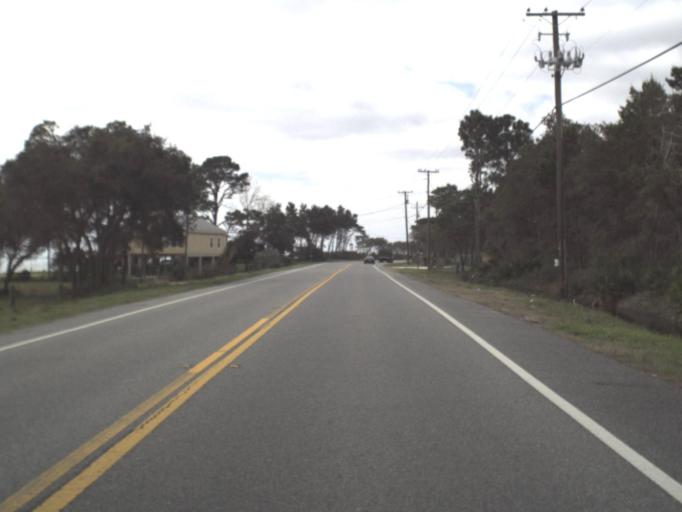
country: US
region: Florida
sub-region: Franklin County
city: Carrabelle
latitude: 29.8231
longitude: -84.7065
